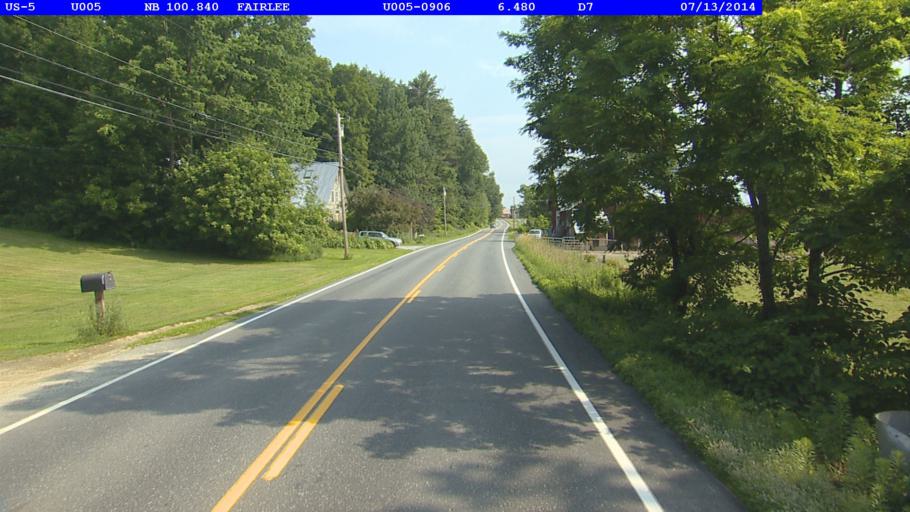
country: US
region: New Hampshire
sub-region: Grafton County
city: Orford
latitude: 43.9501
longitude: -72.1176
